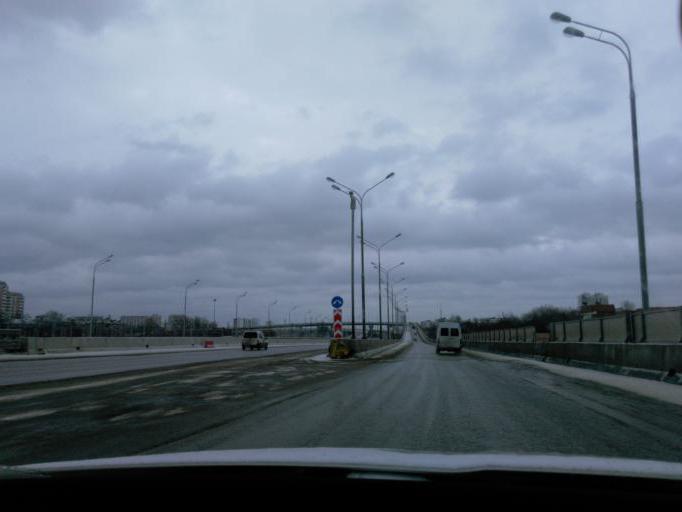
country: RU
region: Moscow
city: Novokhovrino
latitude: 55.8706
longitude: 37.5035
